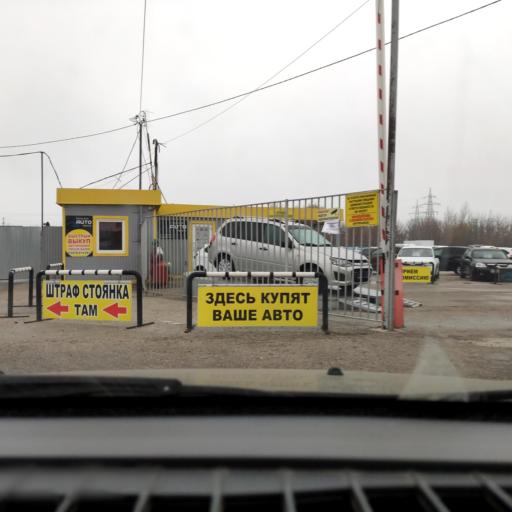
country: RU
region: Samara
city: Tol'yatti
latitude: 53.5420
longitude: 49.4235
